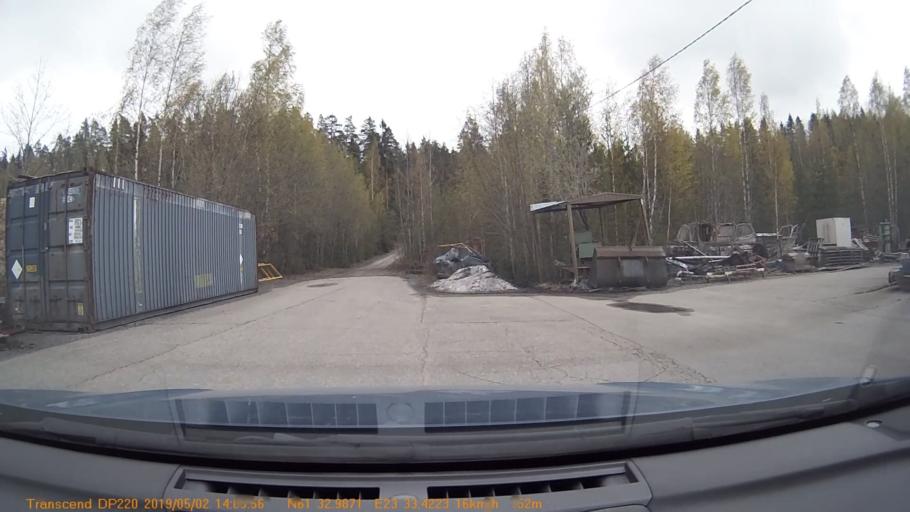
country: FI
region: Pirkanmaa
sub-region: Tampere
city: Yloejaervi
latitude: 61.5498
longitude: 23.5570
